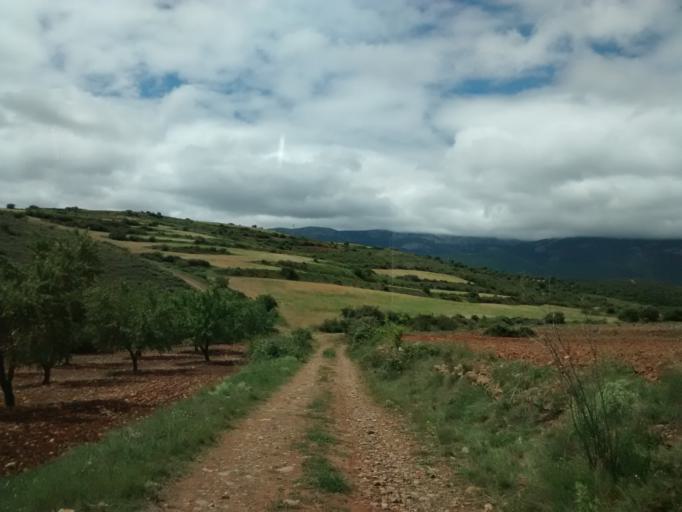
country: ES
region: Aragon
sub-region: Provincia de Zaragoza
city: Trasmoz
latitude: 41.8332
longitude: -1.7413
